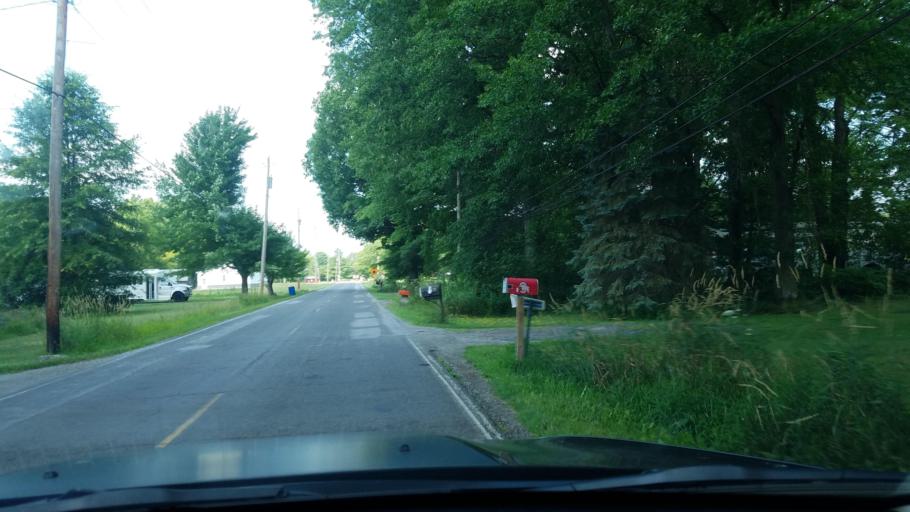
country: US
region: Ohio
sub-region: Trumbull County
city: Champion Heights
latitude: 41.3301
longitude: -80.8071
